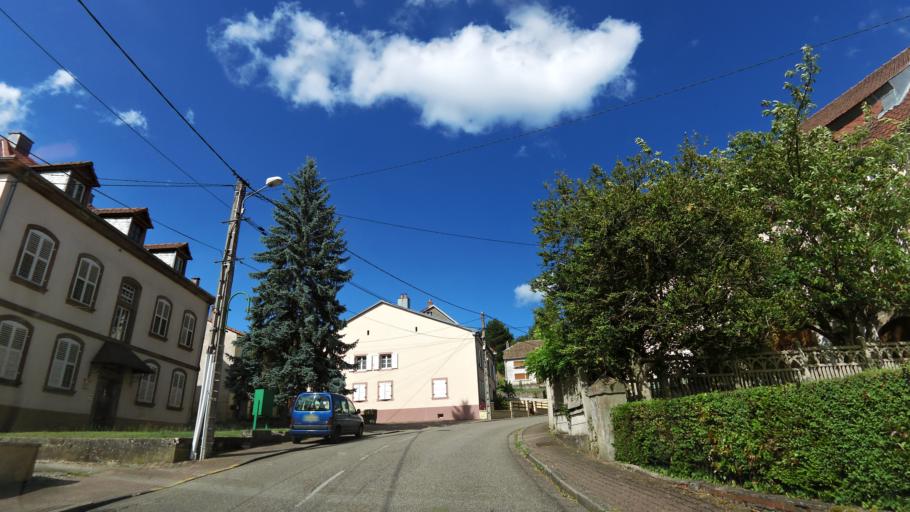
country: FR
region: Lorraine
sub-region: Departement de la Moselle
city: Abreschviller
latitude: 48.6374
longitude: 7.0969
